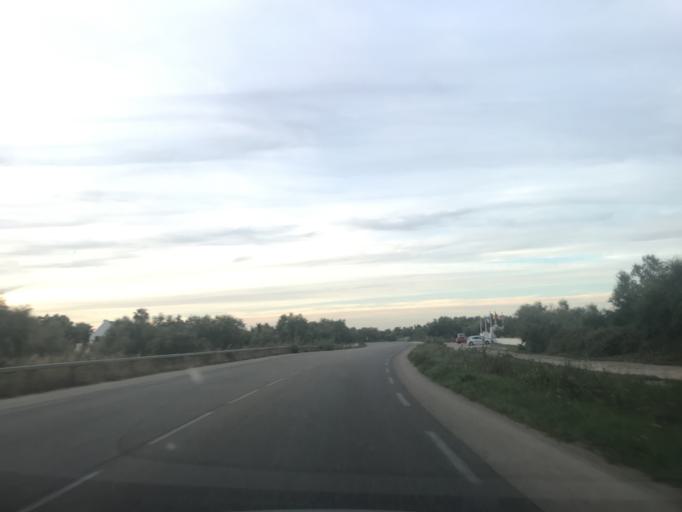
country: FR
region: Provence-Alpes-Cote d'Azur
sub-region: Departement des Bouches-du-Rhone
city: Saintes-Maries-de-la-Mer
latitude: 43.4642
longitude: 4.4192
